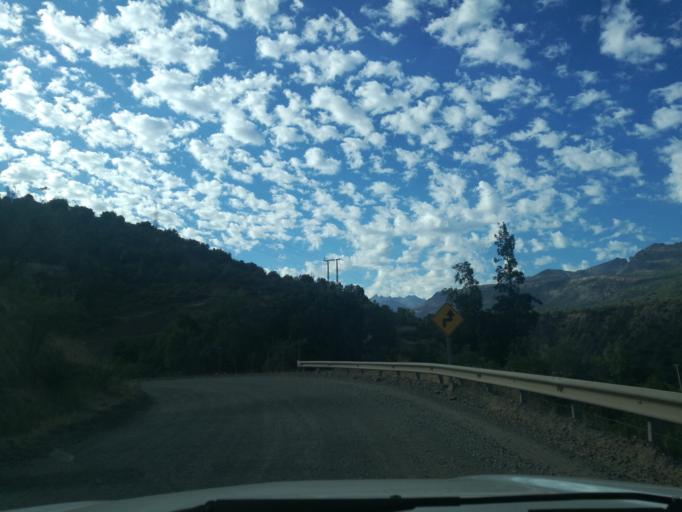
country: CL
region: O'Higgins
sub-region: Provincia de Cachapoal
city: Machali
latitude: -34.2712
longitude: -70.4533
